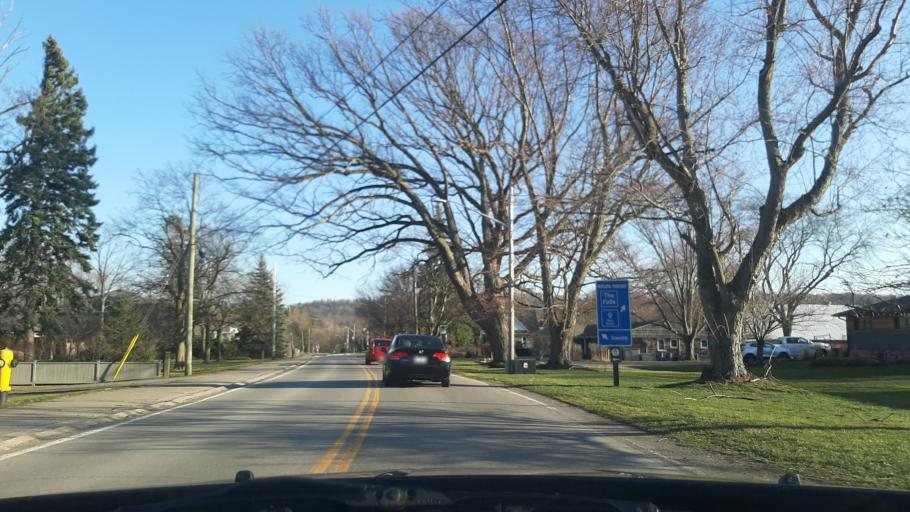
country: US
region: New York
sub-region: Niagara County
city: Lewiston
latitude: 43.1719
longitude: -79.0586
